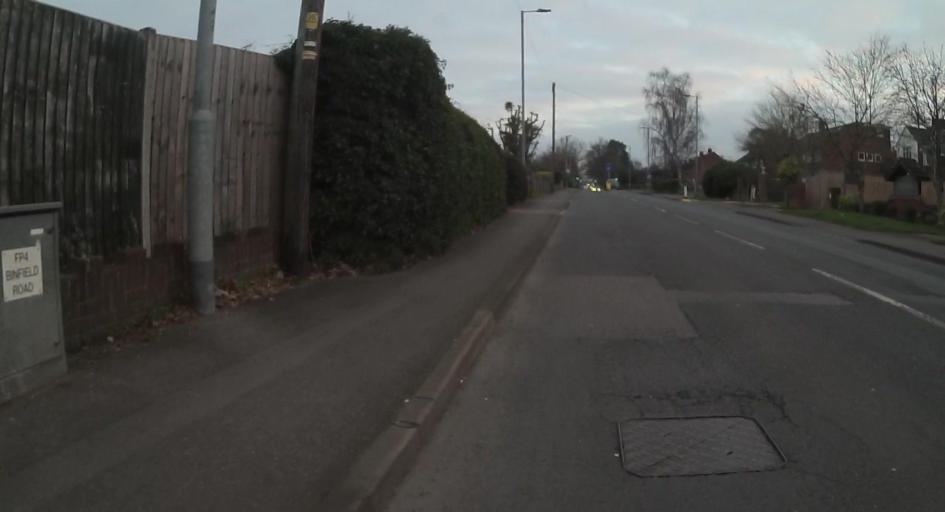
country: GB
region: England
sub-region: Bracknell Forest
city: Bracknell
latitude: 51.4249
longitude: -0.7636
